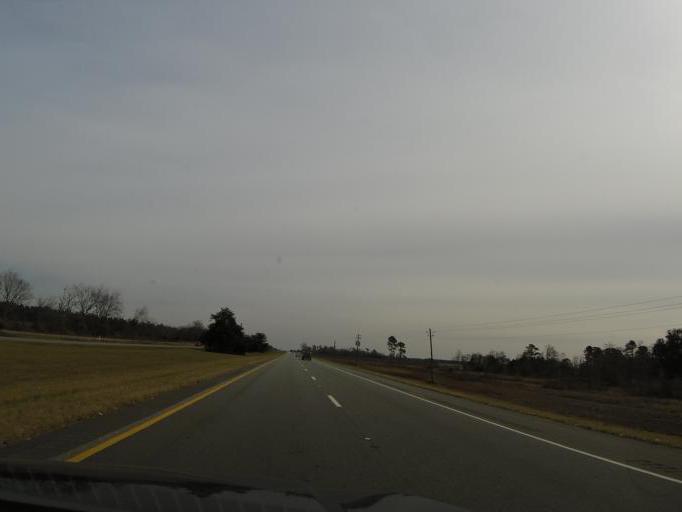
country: US
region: Georgia
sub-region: Seminole County
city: Donalsonville
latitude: 31.0783
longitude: -84.9665
